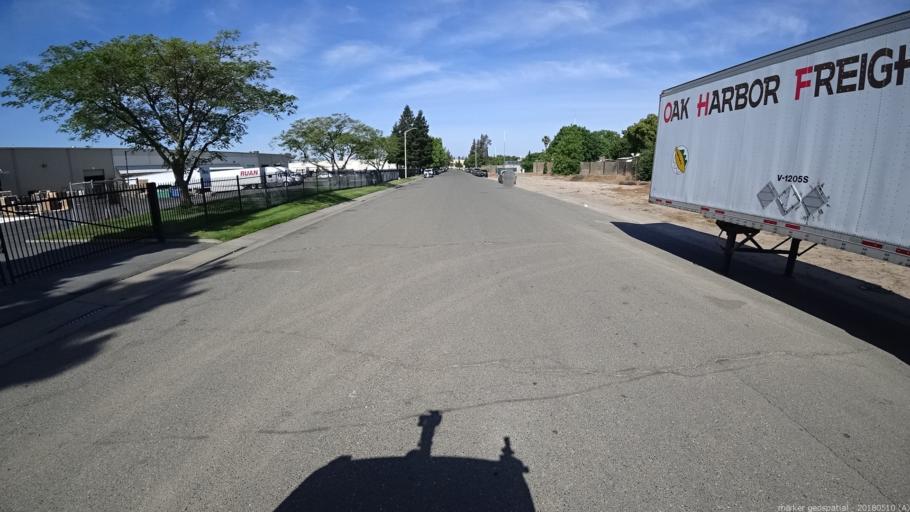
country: US
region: California
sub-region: Sacramento County
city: Rio Linda
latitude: 38.6447
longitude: -121.4664
